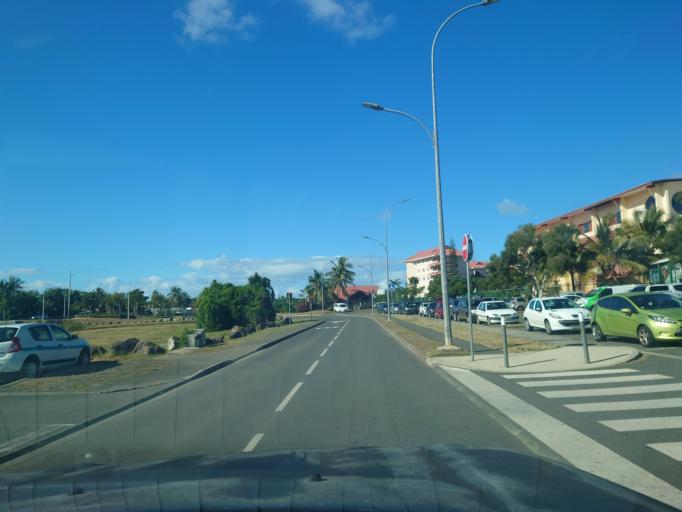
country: NC
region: South Province
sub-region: Noumea
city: Noumea
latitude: -22.2693
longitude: 166.4687
